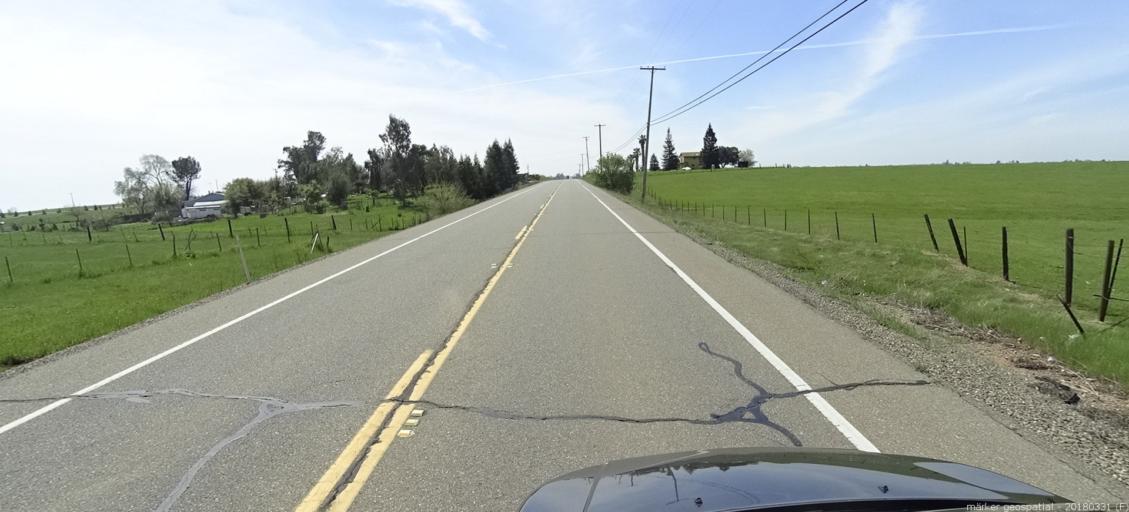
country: US
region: California
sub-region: Sacramento County
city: Wilton
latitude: 38.4975
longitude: -121.2283
